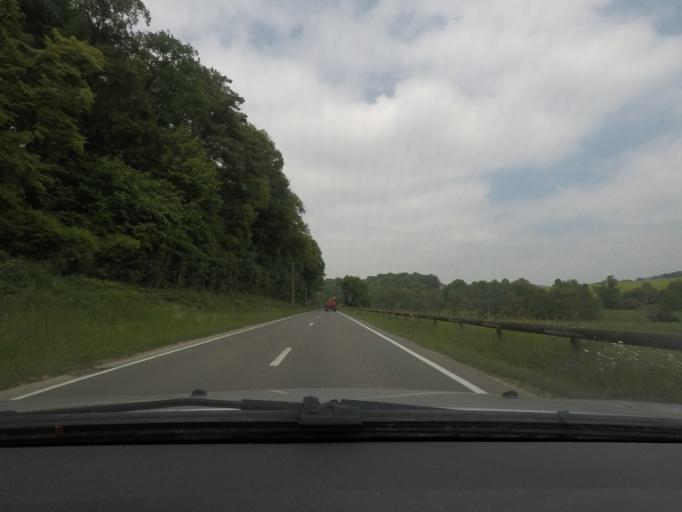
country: BE
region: Wallonia
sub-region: Province de Namur
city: Assesse
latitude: 50.4389
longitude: 5.0088
